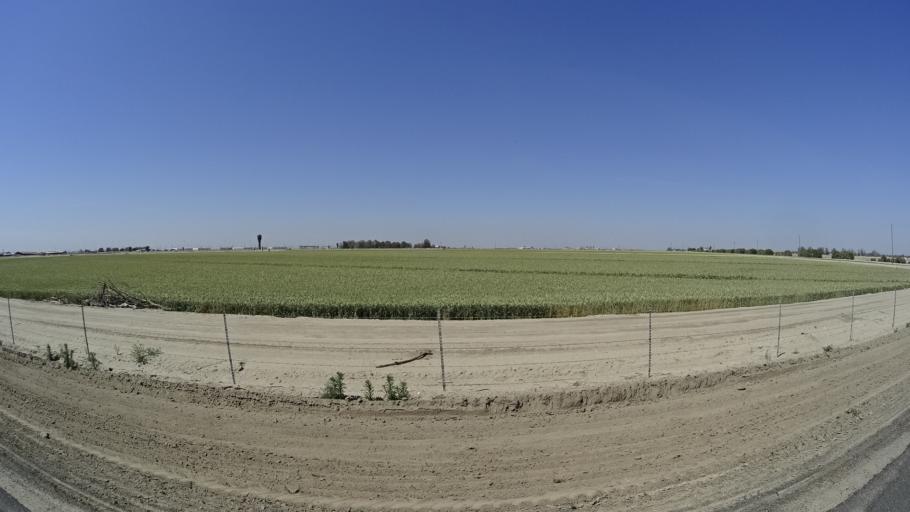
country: US
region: California
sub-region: Kings County
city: Corcoran
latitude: 36.0720
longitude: -119.5386
